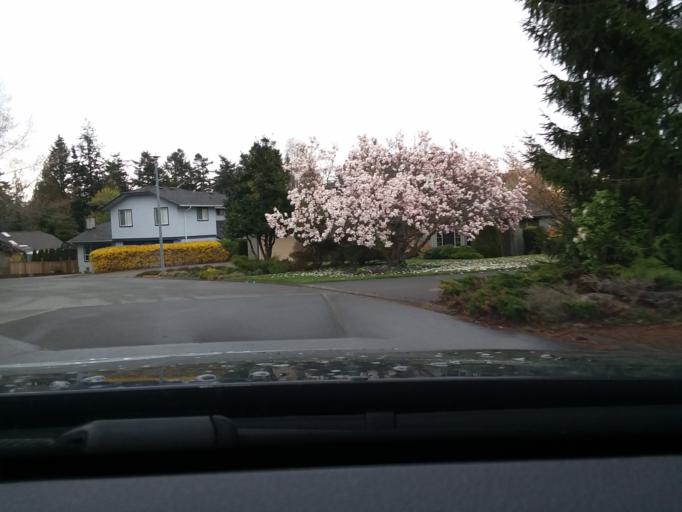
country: CA
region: British Columbia
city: Victoria
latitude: 48.5188
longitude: -123.3797
